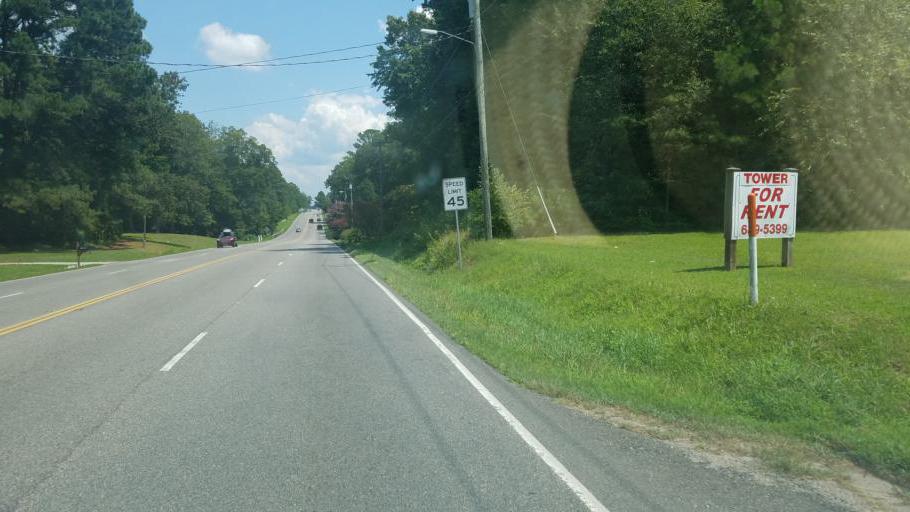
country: US
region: Virginia
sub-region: Isle of Wight County
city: Windsor
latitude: 36.8035
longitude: -76.7246
